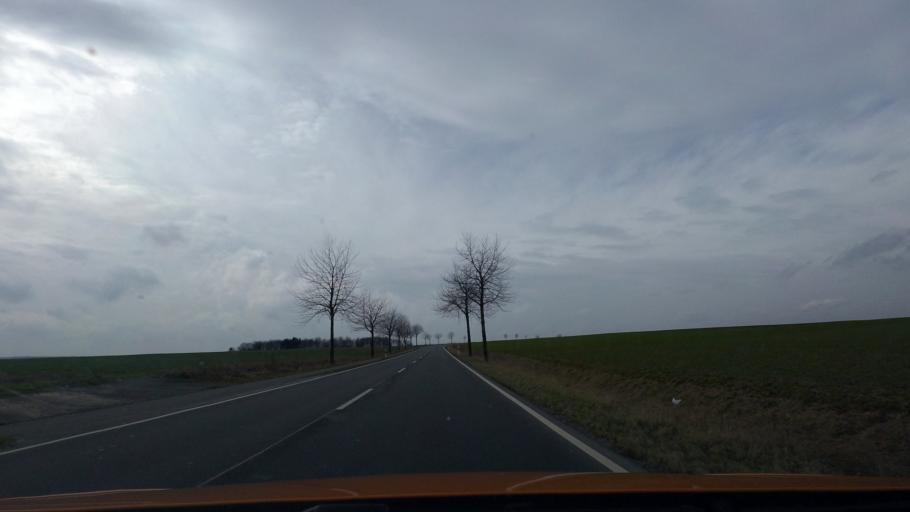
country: DE
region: Lower Saxony
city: Supplingen
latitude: 52.2272
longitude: 10.8862
